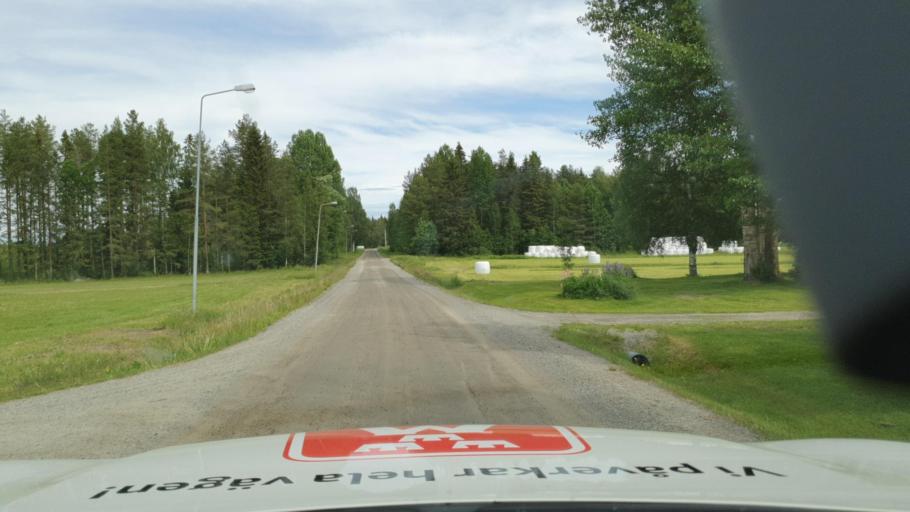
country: SE
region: Vaesterbotten
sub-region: Skelleftea Kommun
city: Viken
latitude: 64.5001
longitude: 20.9151
